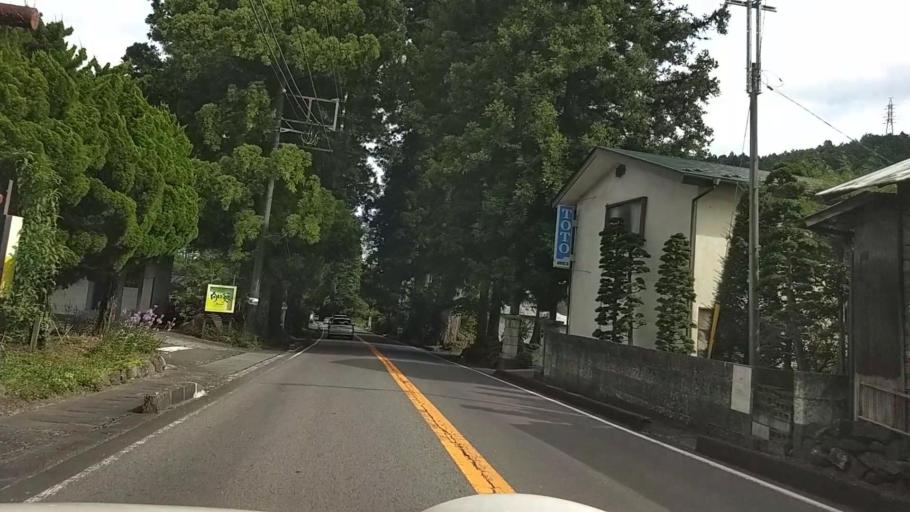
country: JP
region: Tochigi
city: Nikko
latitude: 36.7421
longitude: 139.6307
